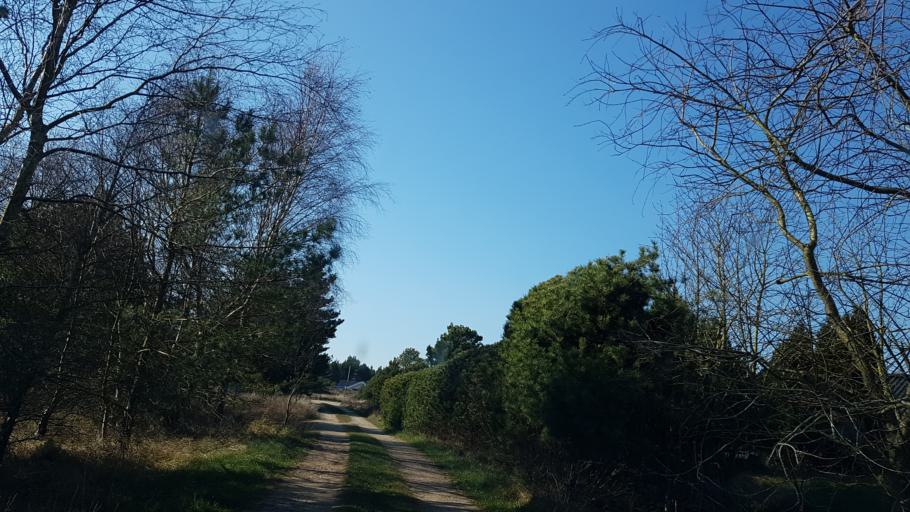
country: DE
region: Schleswig-Holstein
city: List
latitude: 55.1139
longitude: 8.5506
